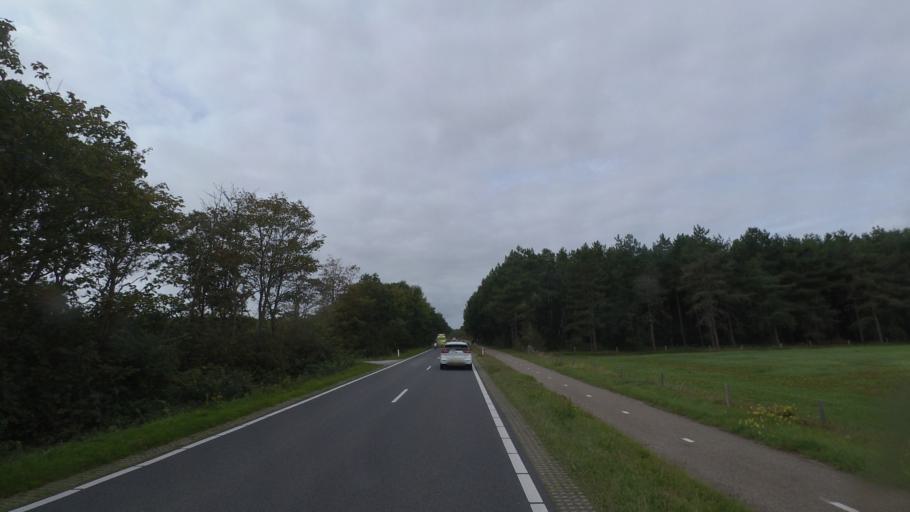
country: NL
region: Friesland
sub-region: Gemeente Ameland
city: Nes
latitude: 53.4454
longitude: 5.7159
